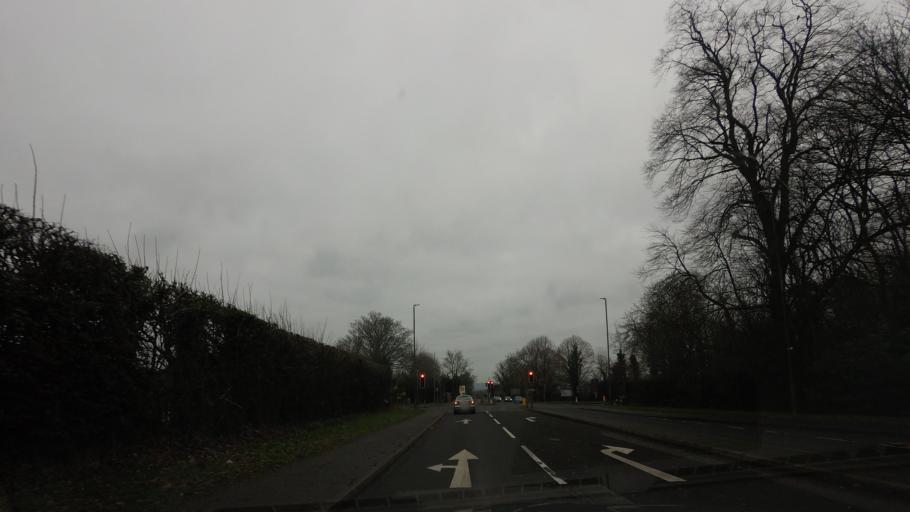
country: GB
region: England
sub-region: Kent
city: Maidstone
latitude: 51.2295
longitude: 0.5126
